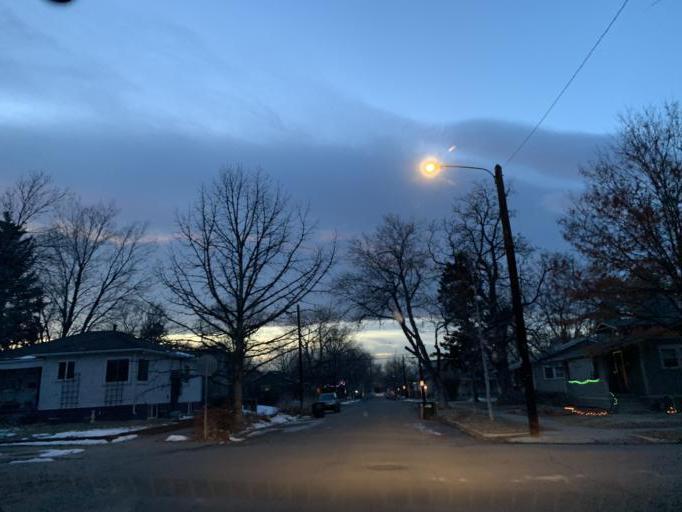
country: US
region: Colorado
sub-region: Jefferson County
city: Edgewater
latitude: 39.7739
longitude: -105.0403
